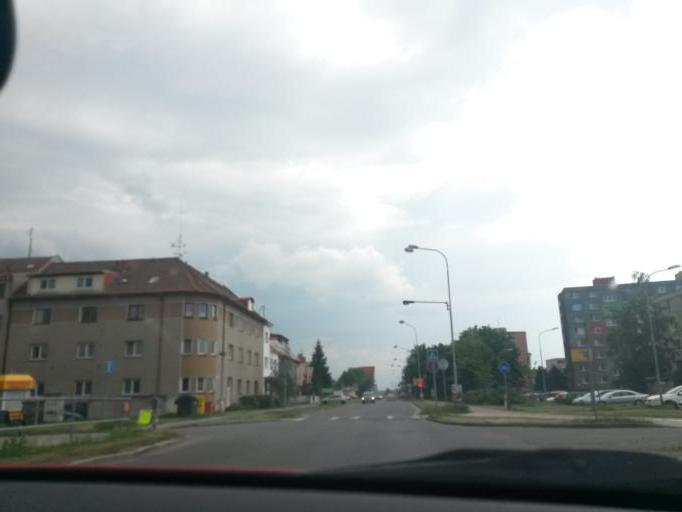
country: CZ
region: Olomoucky
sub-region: Okres Olomouc
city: Olomouc
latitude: 49.5797
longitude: 17.2488
